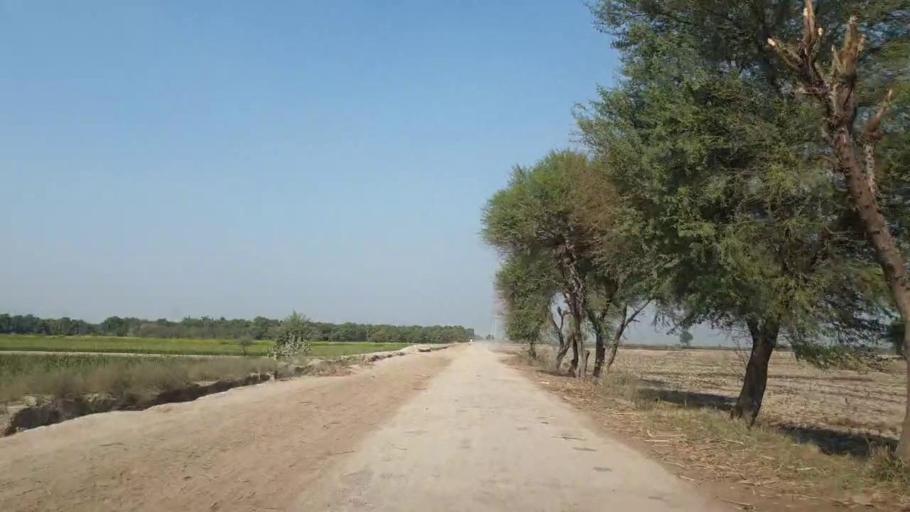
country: PK
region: Sindh
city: Tando Allahyar
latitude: 25.4983
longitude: 68.8221
